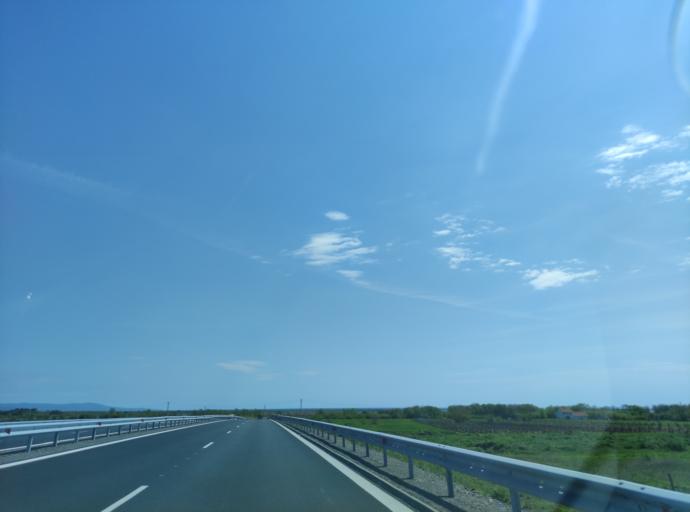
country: BG
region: Burgas
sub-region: Obshtina Pomorie
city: Pomorie
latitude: 42.5897
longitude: 27.6032
